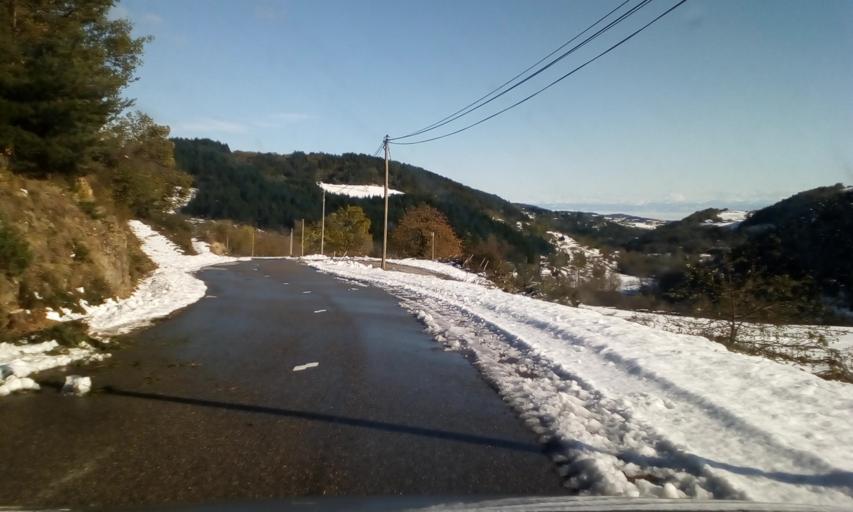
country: FR
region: Rhone-Alpes
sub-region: Departement de l'Ardeche
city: Saint-Felicien
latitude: 45.0810
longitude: 4.5757
